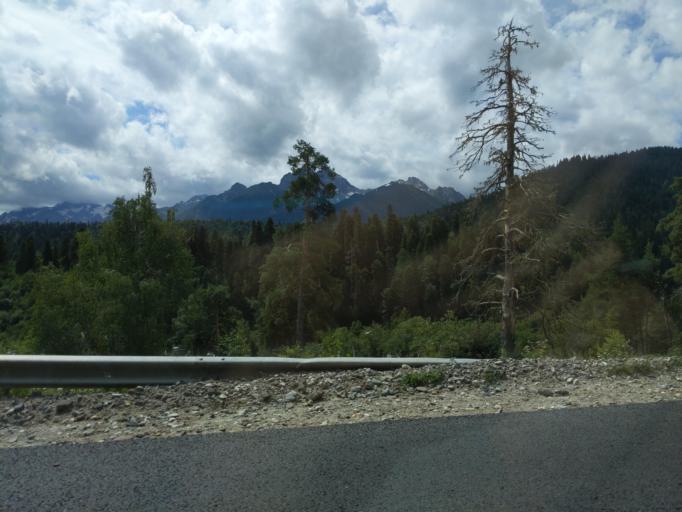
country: RU
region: Karachayevo-Cherkesiya
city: Nizhniy Arkhyz
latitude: 43.5369
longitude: 41.2185
